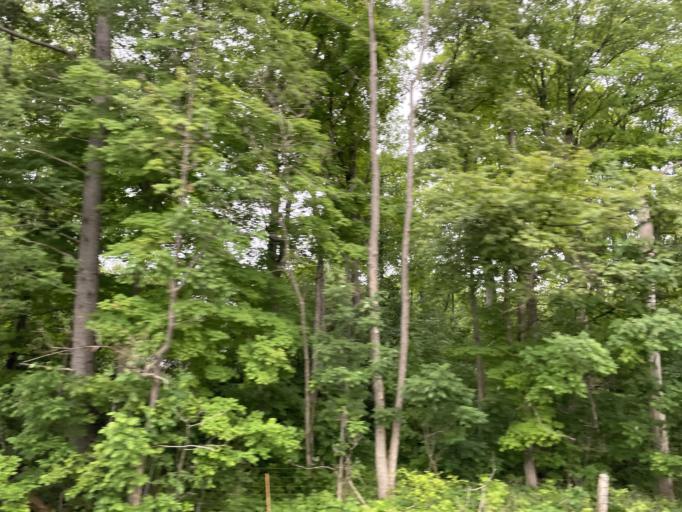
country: CA
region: Ontario
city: Cambridge
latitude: 43.4442
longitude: -80.2584
